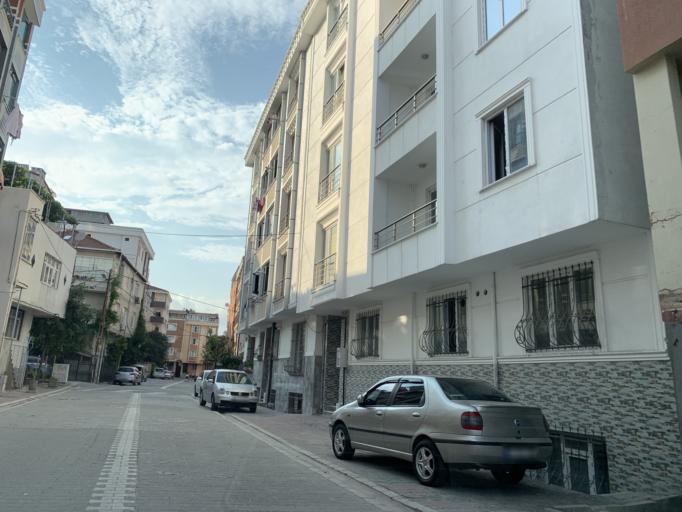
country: TR
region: Istanbul
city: Esenyurt
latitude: 41.0403
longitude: 28.6820
